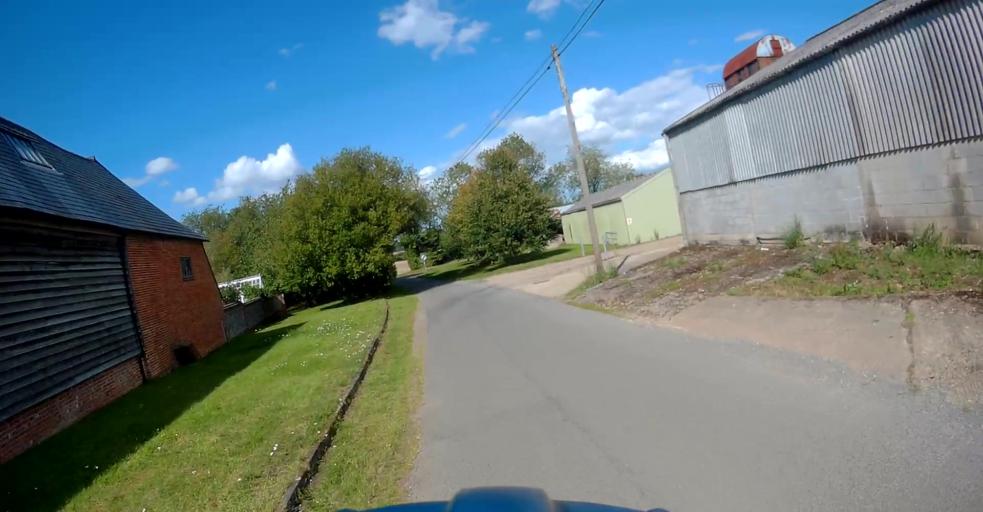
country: GB
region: England
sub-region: Hampshire
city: Four Marks
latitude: 51.1599
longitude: -1.0912
